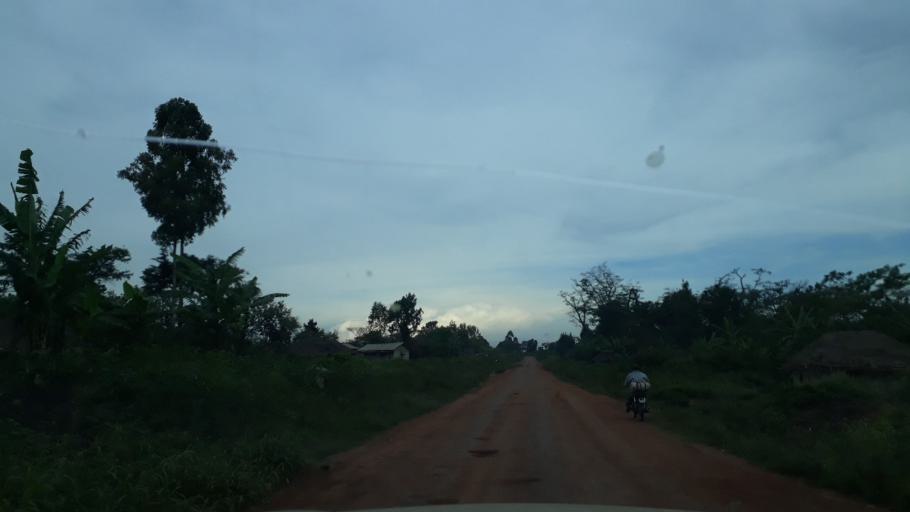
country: UG
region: Northern Region
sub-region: Zombo District
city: Paidha
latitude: 2.1773
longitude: 30.7109
